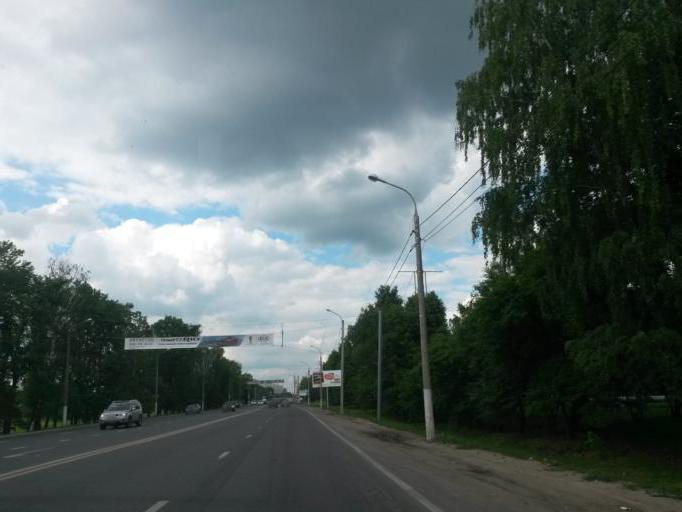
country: RU
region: Moskovskaya
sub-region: Chekhovskiy Rayon
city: Chekhov
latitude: 55.1572
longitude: 37.4639
